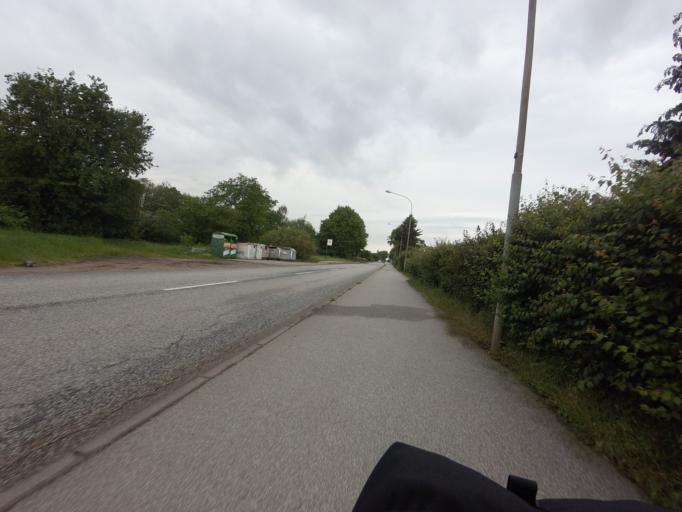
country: DE
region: Schleswig-Holstein
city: Ratekau
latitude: 53.9122
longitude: 10.7486
